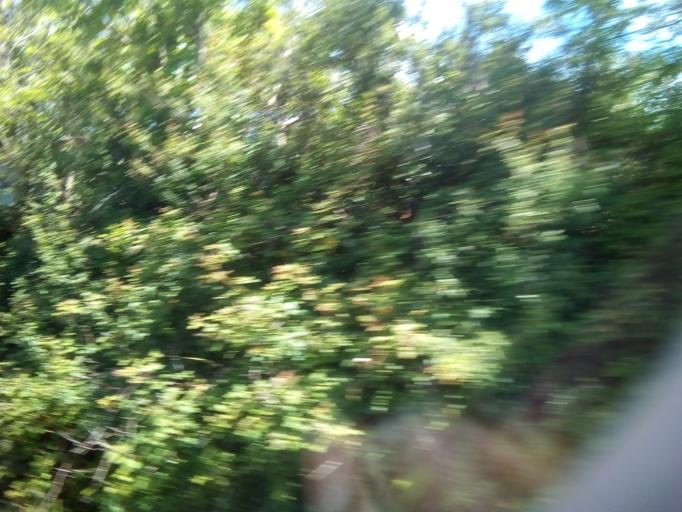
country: IE
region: Leinster
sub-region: Loch Garman
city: Loch Garman
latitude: 52.2377
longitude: -6.5989
